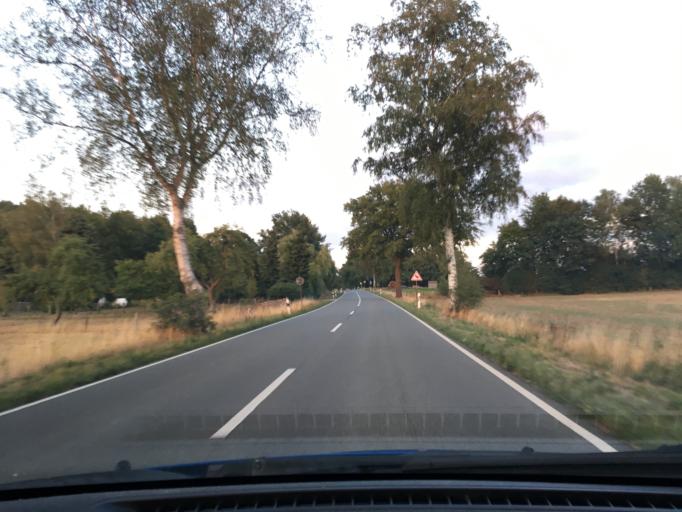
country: DE
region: Lower Saxony
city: Hitzacker
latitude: 53.1467
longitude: 11.0074
